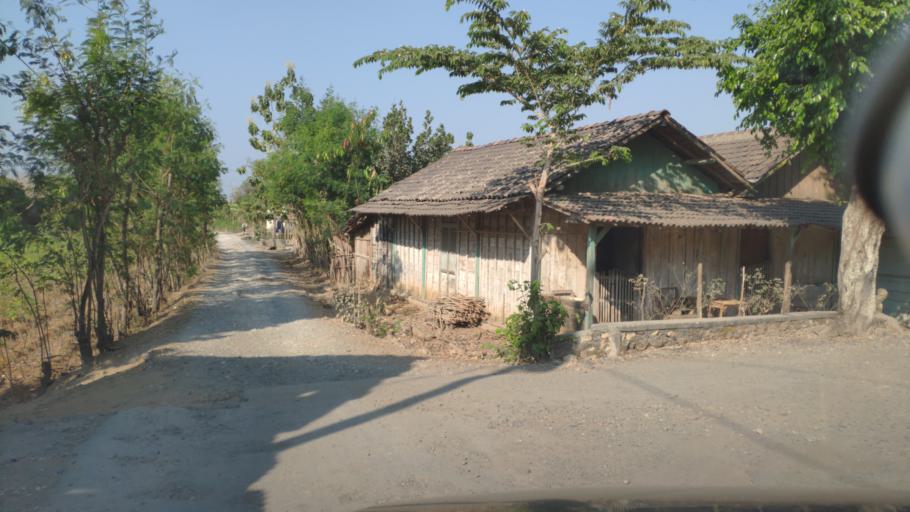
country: ID
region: Central Java
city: Ketringan
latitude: -6.9531
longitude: 111.5510
